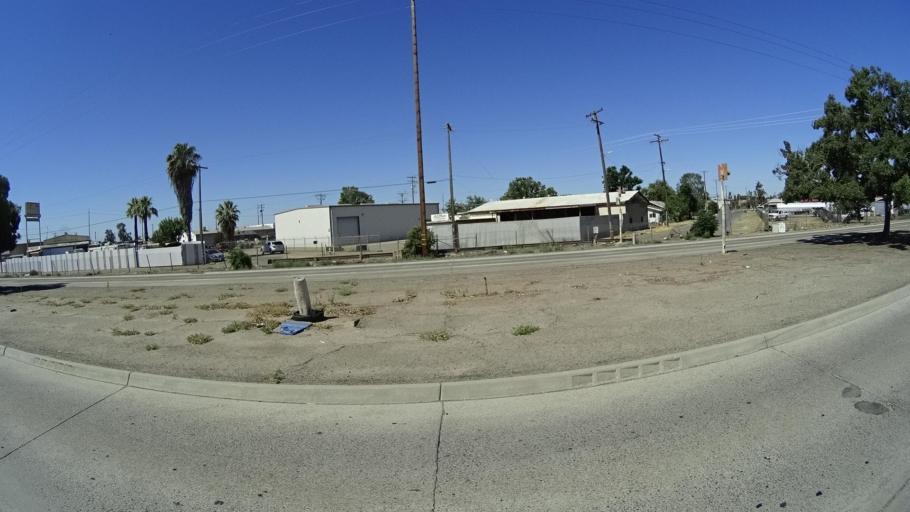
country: US
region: California
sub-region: Fresno County
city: Fresno
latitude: 36.7161
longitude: -119.7781
